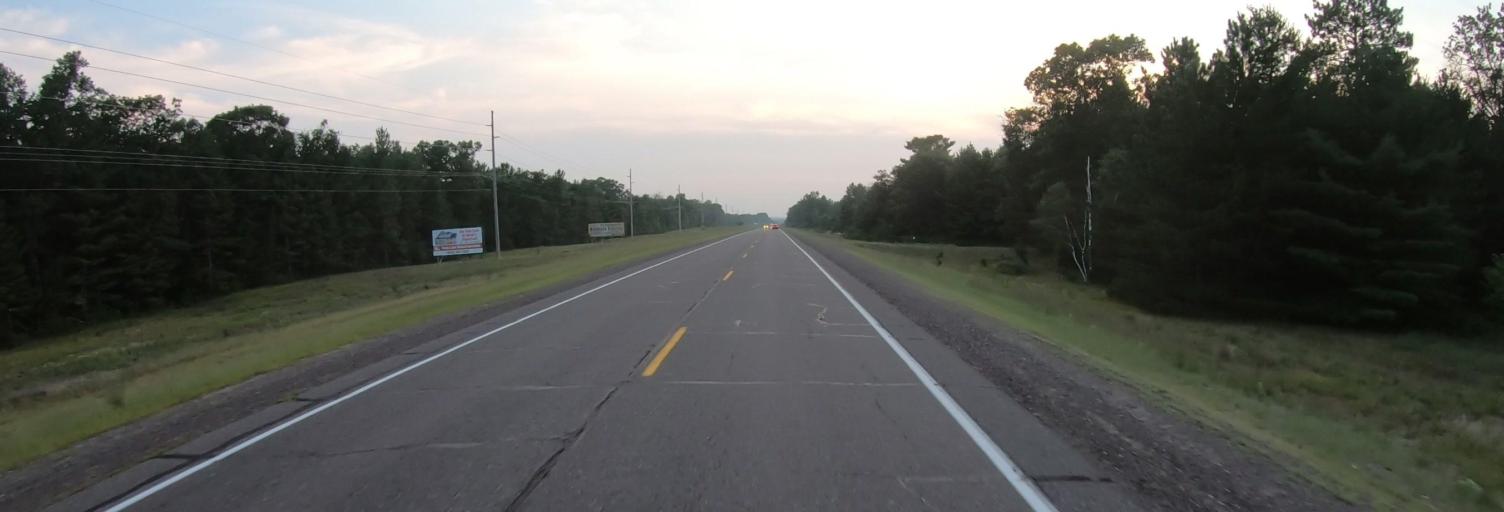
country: US
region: Wisconsin
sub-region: Burnett County
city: Grantsburg
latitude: 45.7731
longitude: -92.7446
